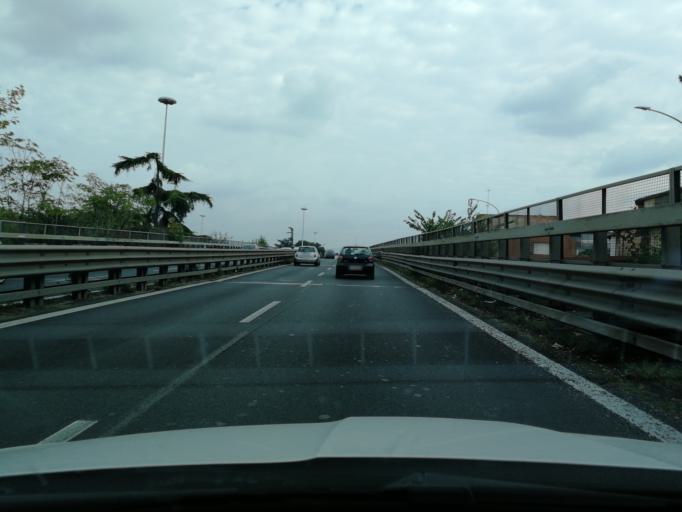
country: IT
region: Latium
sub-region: Citta metropolitana di Roma Capitale
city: Ciampino
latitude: 41.8441
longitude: 12.5821
